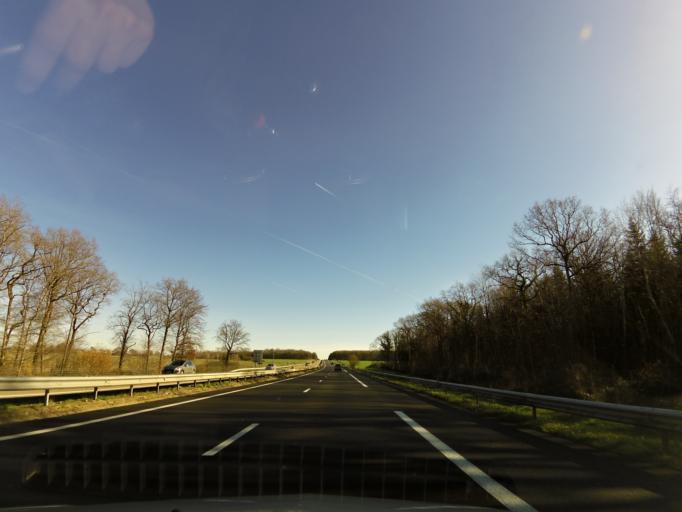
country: FR
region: Bourgogne
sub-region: Departement de l'Yonne
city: Vermenton
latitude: 47.7144
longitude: 3.7712
